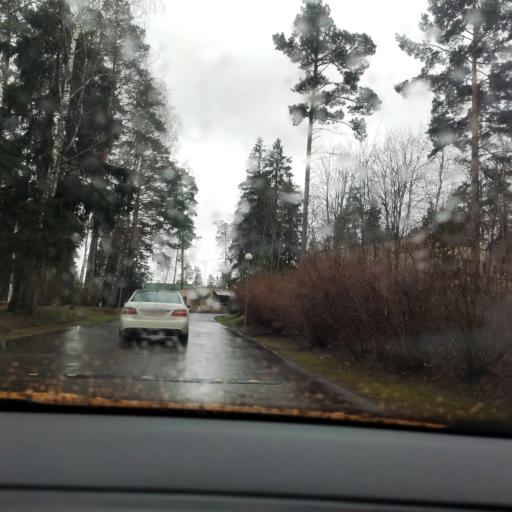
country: RU
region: Moskovskaya
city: Nikolina Gora
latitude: 55.7240
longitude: 36.9646
